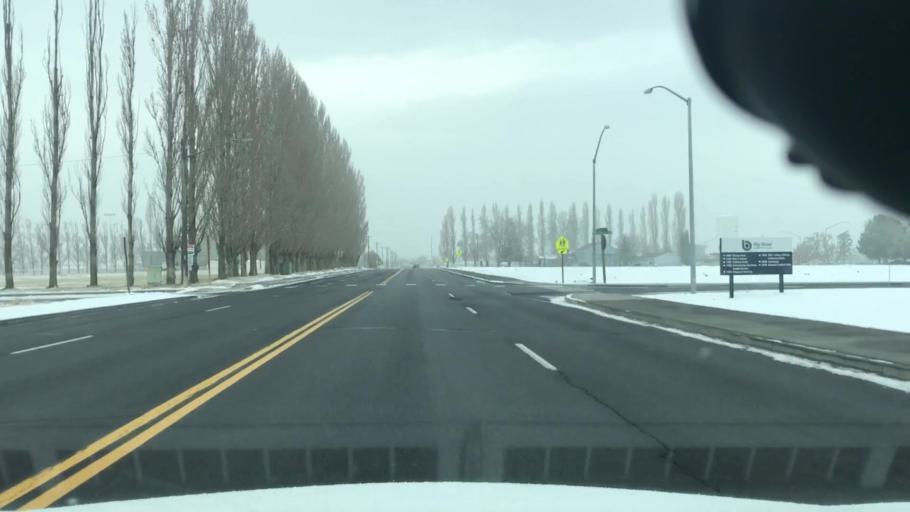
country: US
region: Washington
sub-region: Grant County
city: Moses Lake North
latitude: 47.1864
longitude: -119.3227
